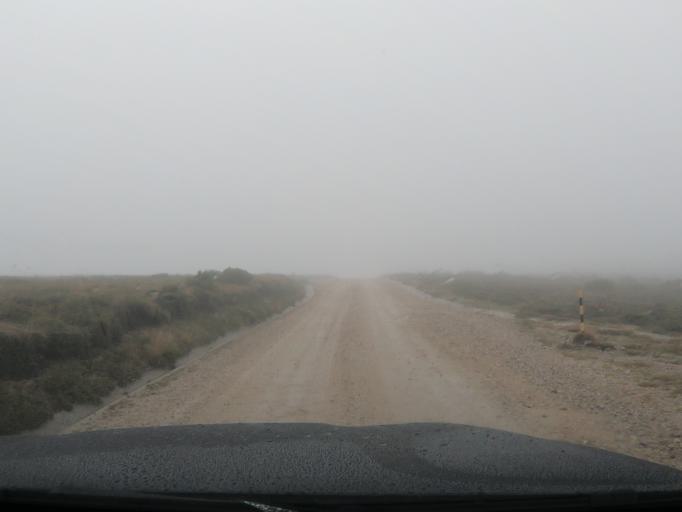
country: PT
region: Vila Real
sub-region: Vila Real
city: Vila Real
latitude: 41.3308
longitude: -7.8358
